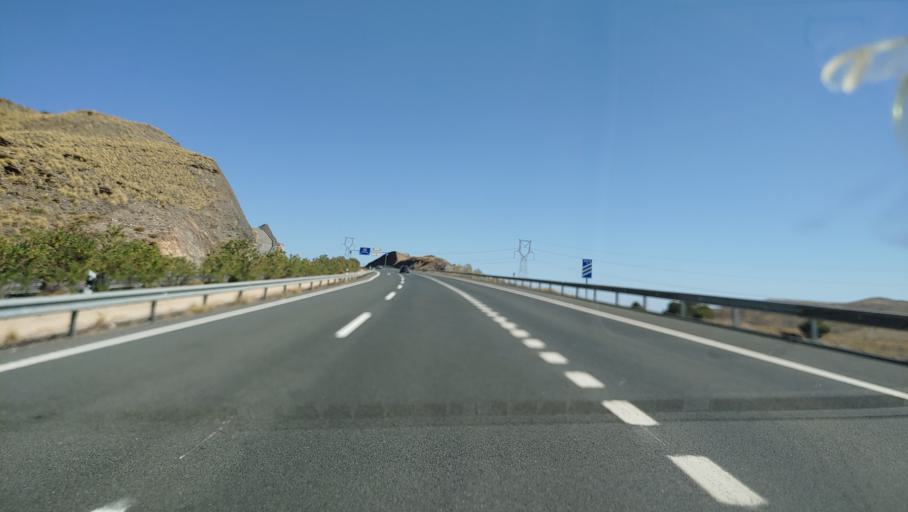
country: ES
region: Andalusia
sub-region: Provincia de Almeria
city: Gergal
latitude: 37.1279
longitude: -2.6371
